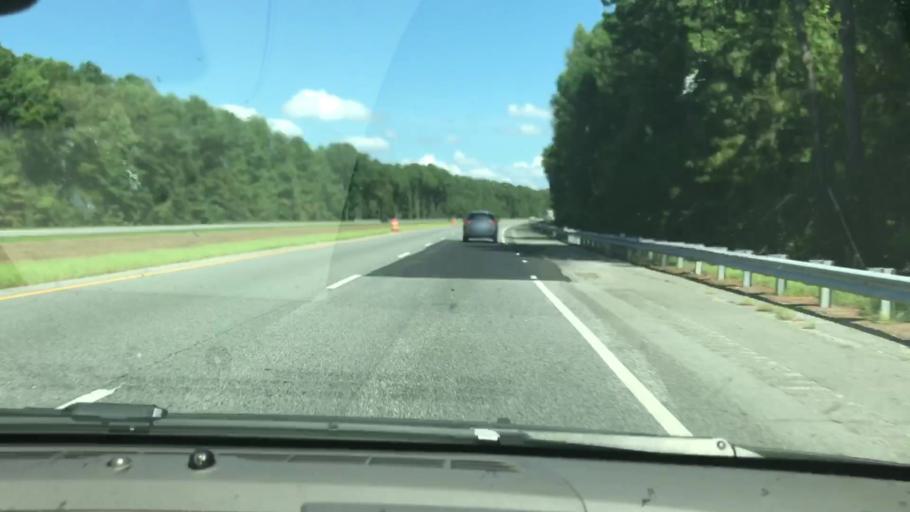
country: US
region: Georgia
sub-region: Harris County
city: Hamilton
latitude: 32.6692
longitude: -84.9858
